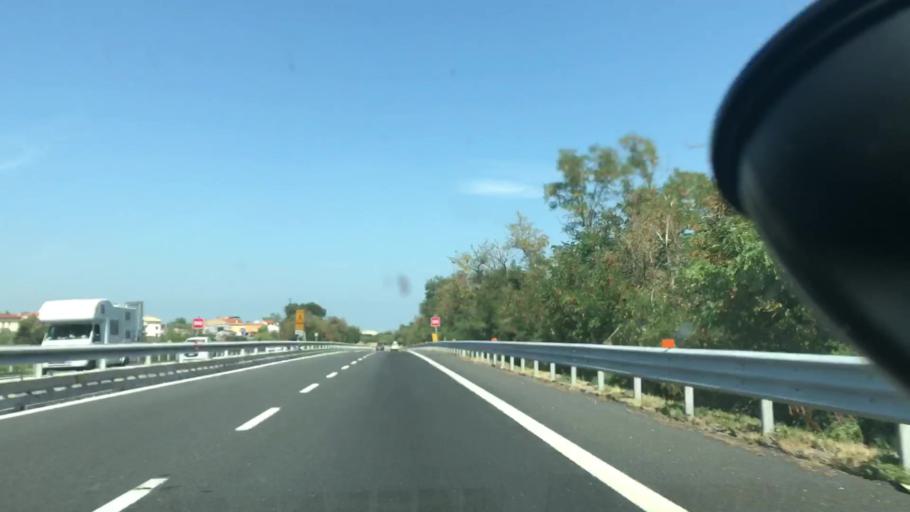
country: IT
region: Abruzzo
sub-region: Provincia di Chieti
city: Vasto
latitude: 42.0994
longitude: 14.6972
